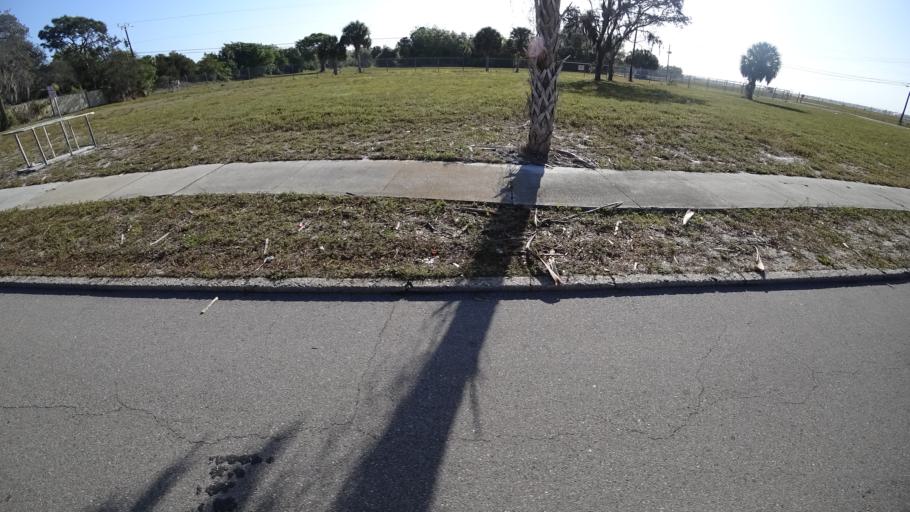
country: US
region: Florida
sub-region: Manatee County
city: Whitfield
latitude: 27.4081
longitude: -82.5678
